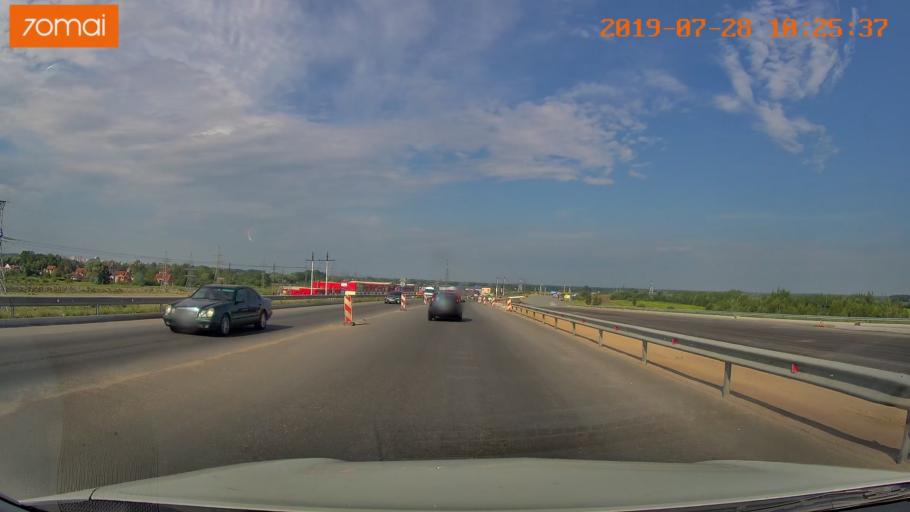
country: RU
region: Kaliningrad
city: Maloye Isakovo
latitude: 54.7678
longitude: 20.5400
